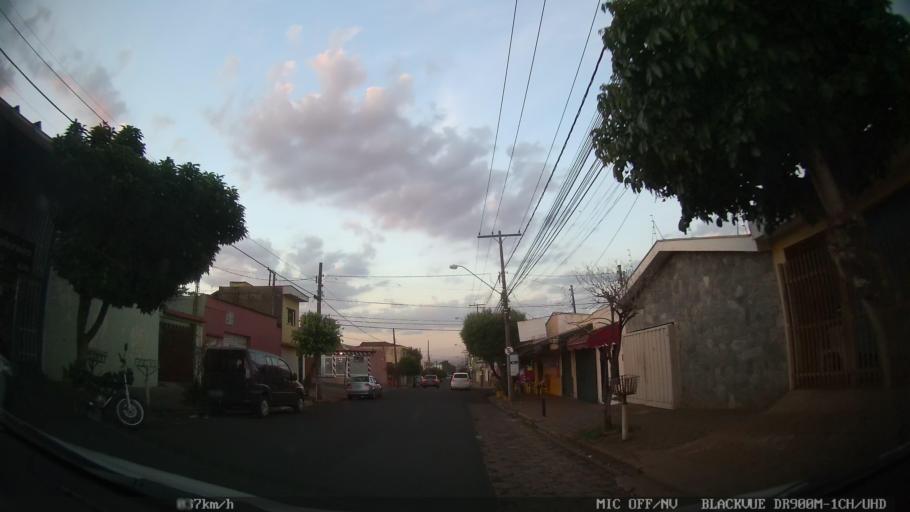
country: BR
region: Sao Paulo
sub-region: Ribeirao Preto
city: Ribeirao Preto
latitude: -21.1541
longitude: -47.8268
